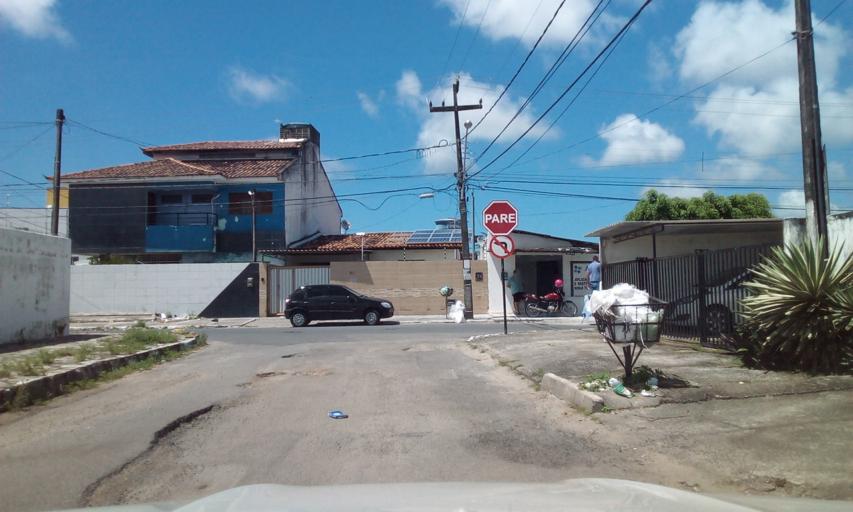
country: BR
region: Paraiba
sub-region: Joao Pessoa
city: Joao Pessoa
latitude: -7.1732
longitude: -34.8613
